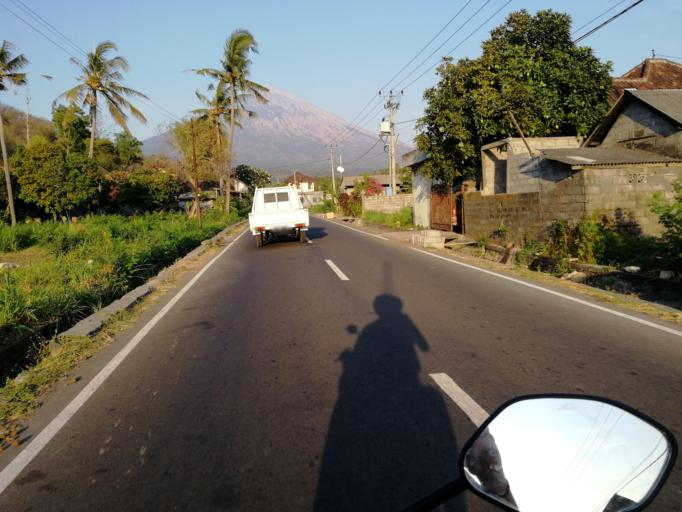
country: ID
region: Bali
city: Biaslantang Kaler
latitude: -8.3365
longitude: 115.6268
